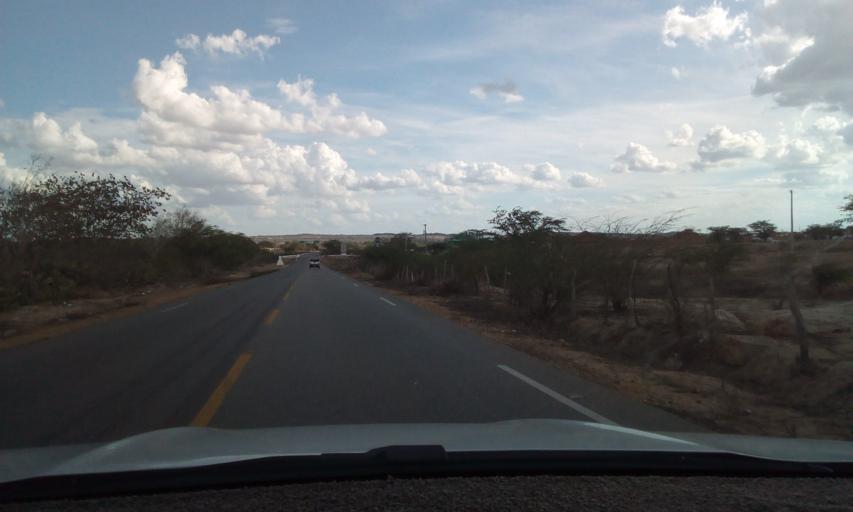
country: BR
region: Paraiba
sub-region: Soledade
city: Soledade
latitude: -6.9351
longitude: -36.3861
